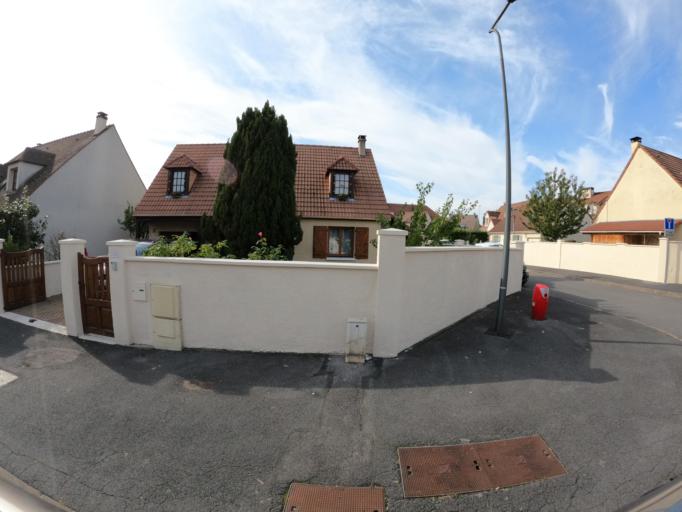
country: FR
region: Ile-de-France
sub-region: Departement de Seine-et-Marne
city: Pontault-Combault
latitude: 48.7846
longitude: 2.6114
